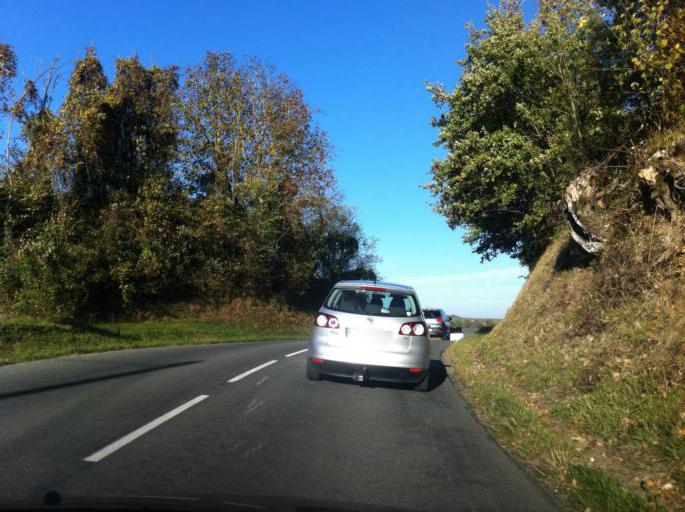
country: FR
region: Aquitaine
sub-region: Departement de la Dordogne
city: Saint-Aulaye
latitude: 45.2613
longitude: 0.2081
